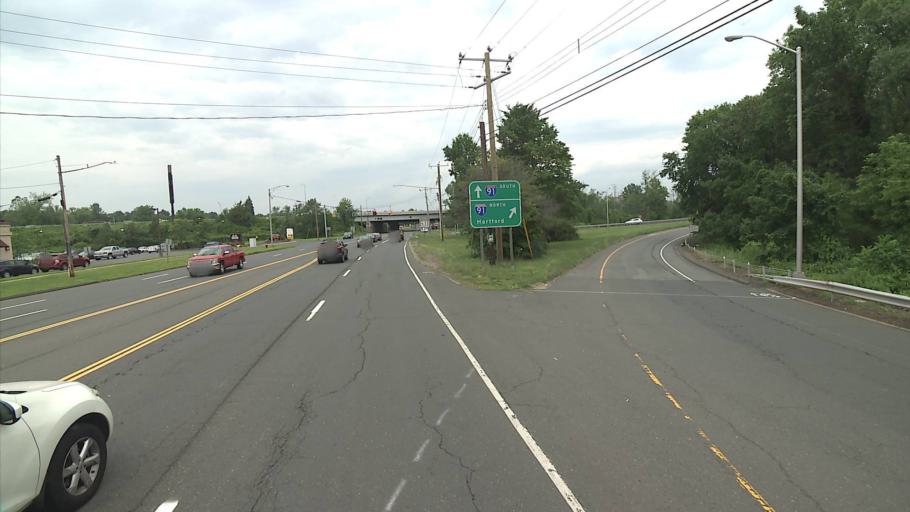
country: US
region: Connecticut
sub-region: Hartford County
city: Wethersfield
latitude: 41.6788
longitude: -72.6524
